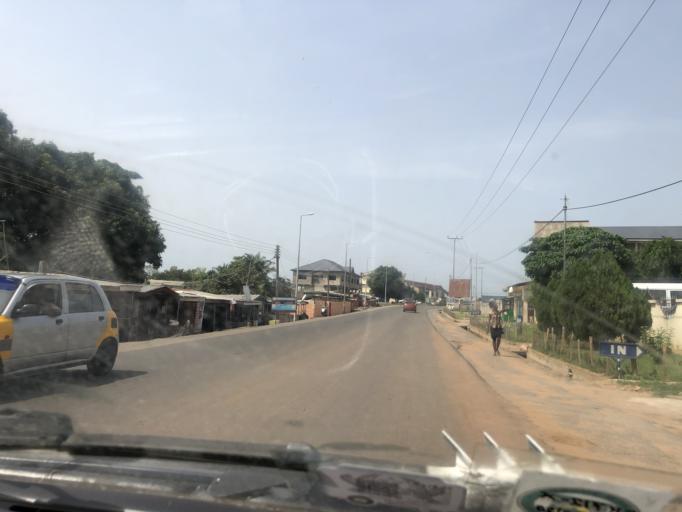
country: GH
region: Eastern
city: Koforidua
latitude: 6.0935
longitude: -0.2696
